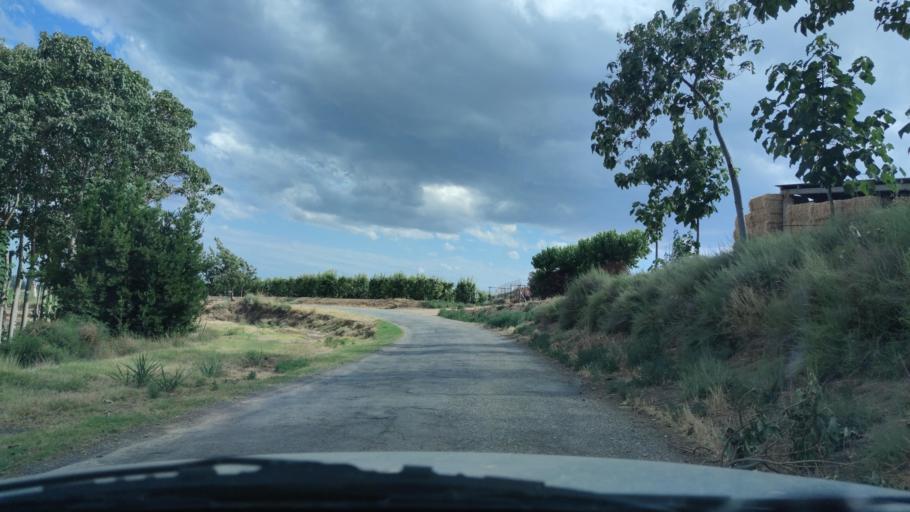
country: ES
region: Catalonia
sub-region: Provincia de Lleida
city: Alcarras
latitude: 41.6044
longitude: 0.5431
